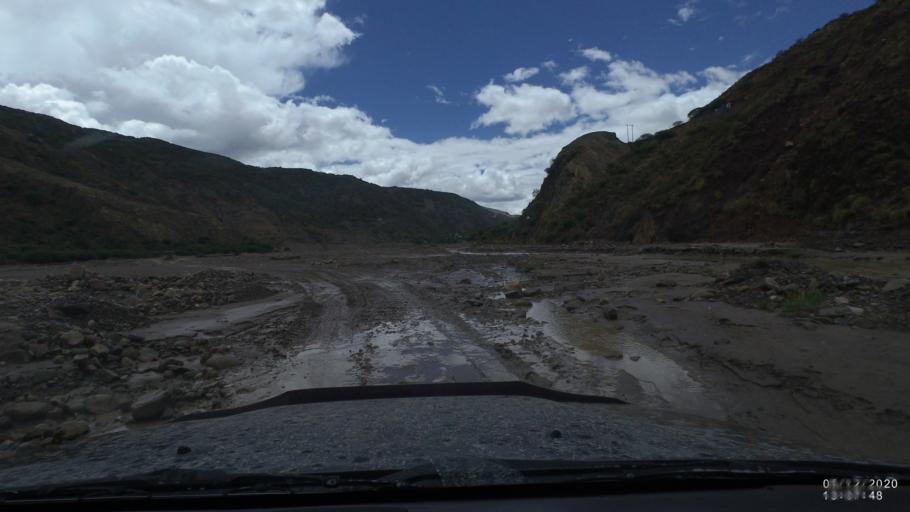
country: BO
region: Cochabamba
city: Sipe Sipe
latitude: -17.5606
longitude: -66.4496
